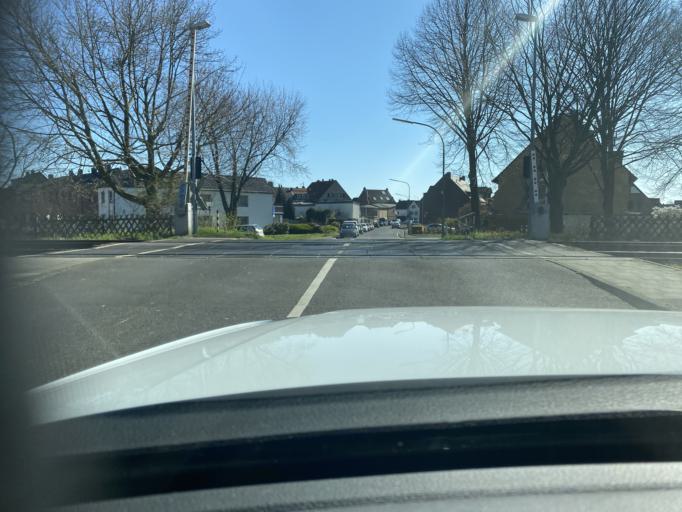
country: DE
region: North Rhine-Westphalia
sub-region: Regierungsbezirk Dusseldorf
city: Neubrueck
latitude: 51.1632
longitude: 6.6628
